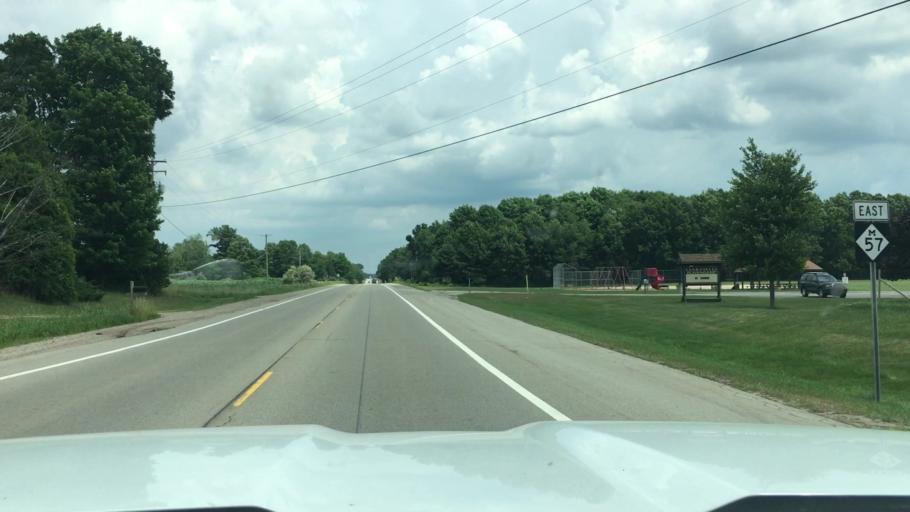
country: US
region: Michigan
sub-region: Kent County
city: Cedar Springs
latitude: 43.1763
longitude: -85.4161
